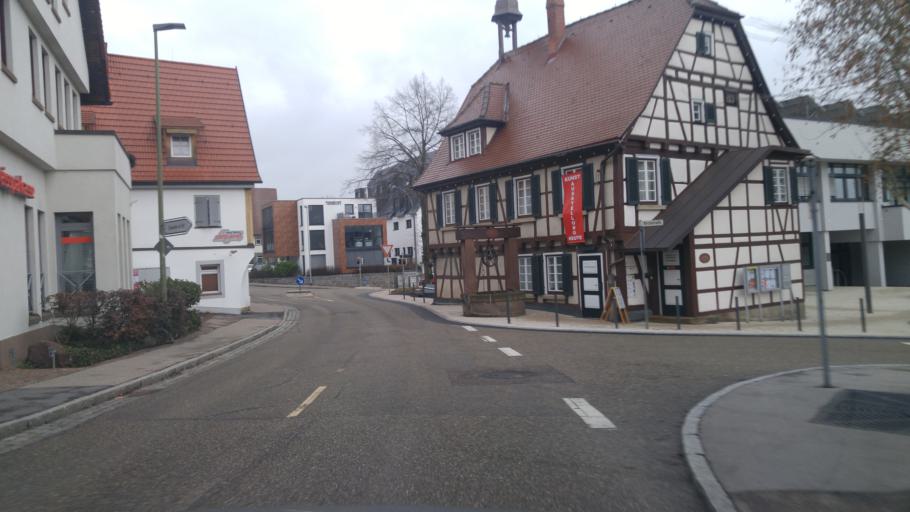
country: DE
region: Baden-Wuerttemberg
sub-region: Regierungsbezirk Stuttgart
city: Leonberg
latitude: 48.8168
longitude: 9.0164
